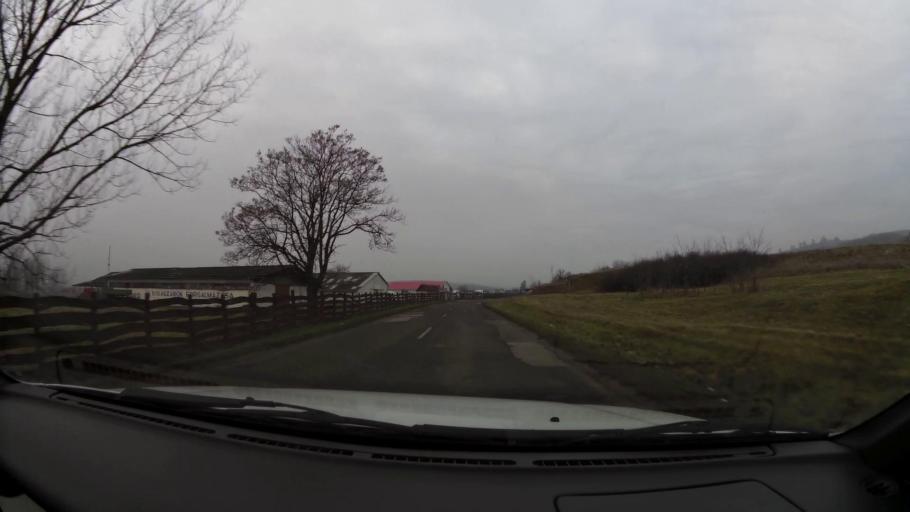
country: HU
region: Borsod-Abauj-Zemplen
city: Izsofalva
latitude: 48.2966
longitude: 20.6569
